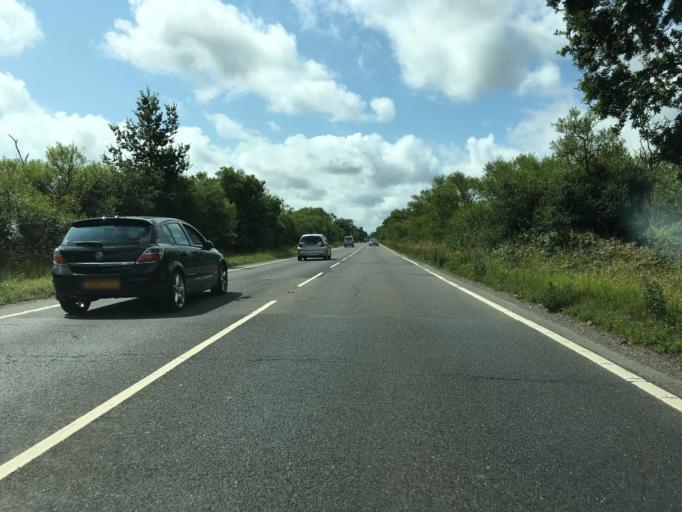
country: GB
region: England
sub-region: East Sussex
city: Pevensey
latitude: 50.8430
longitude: 0.3717
